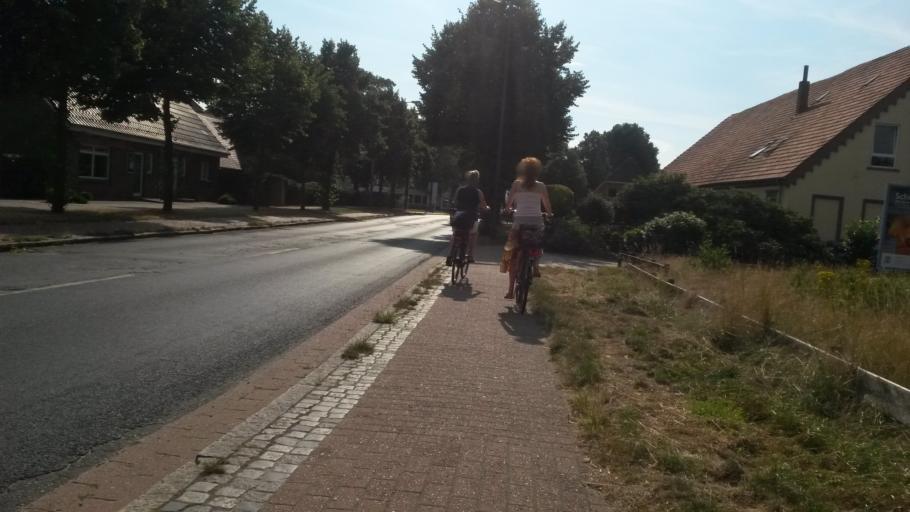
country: DE
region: Lower Saxony
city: Riede
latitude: 53.0386
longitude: 8.9378
